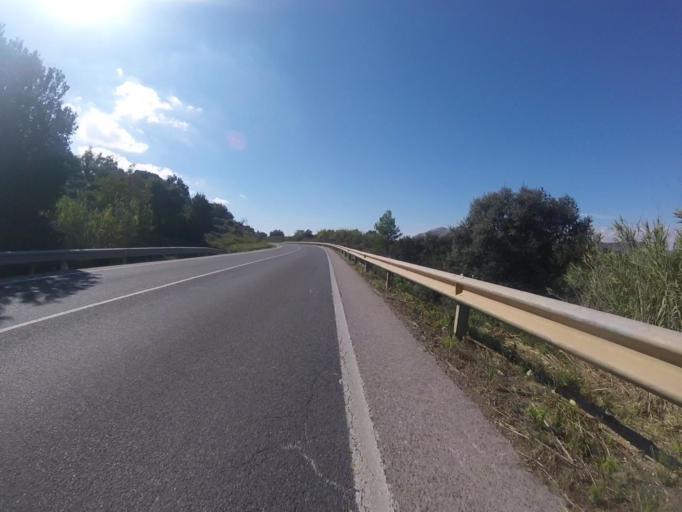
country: ES
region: Valencia
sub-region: Provincia de Castello
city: Sarratella
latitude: 40.3315
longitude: -0.0149
